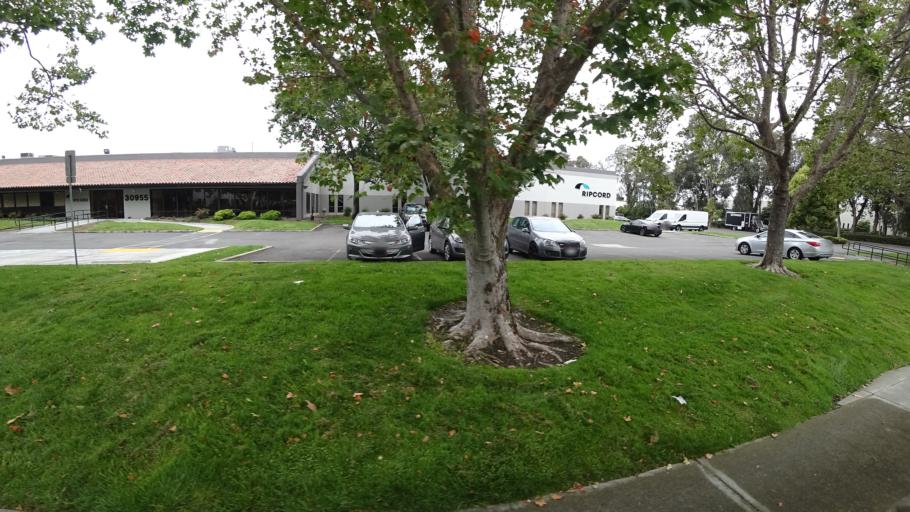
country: US
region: California
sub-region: Alameda County
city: Union City
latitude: 37.6137
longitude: -122.0550
